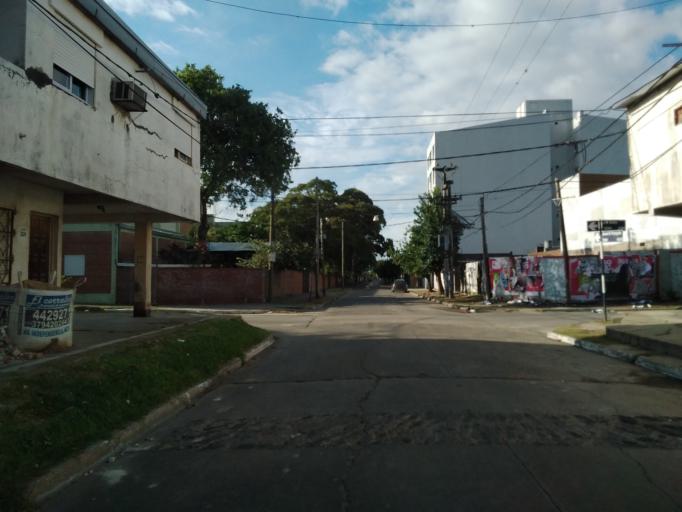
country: AR
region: Corrientes
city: Corrientes
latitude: -27.4618
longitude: -58.8217
